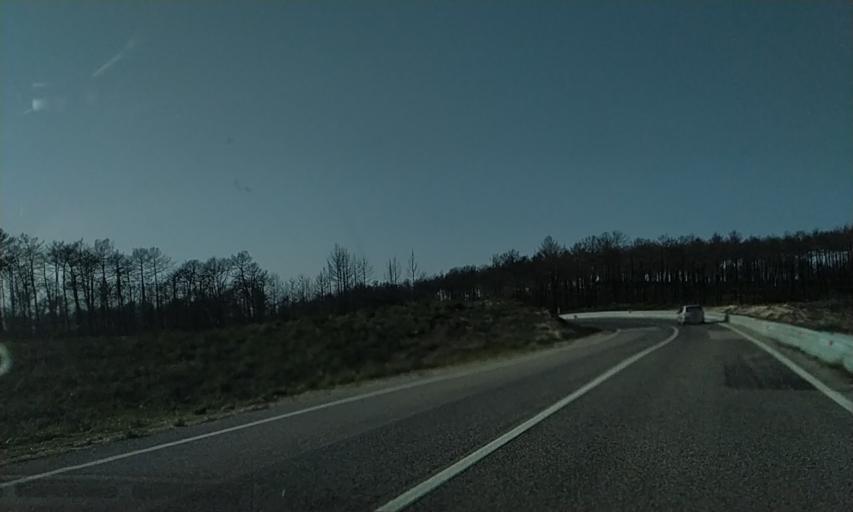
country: PT
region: Leiria
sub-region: Marinha Grande
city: Marinha Grande
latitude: 39.7495
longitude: -9.0094
